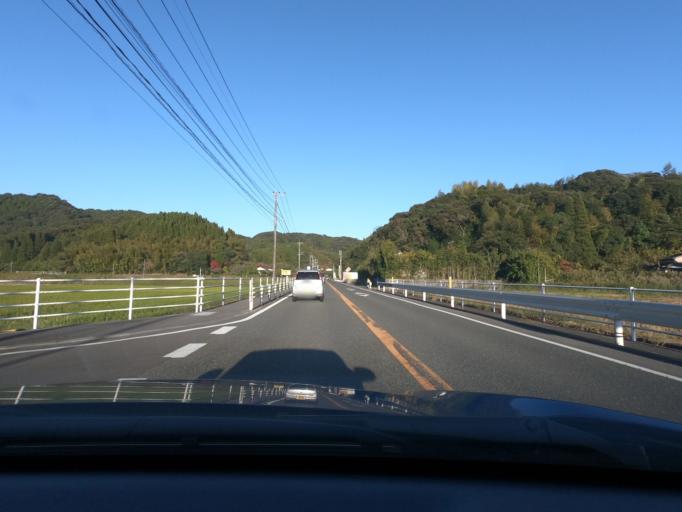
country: JP
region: Kagoshima
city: Satsumasendai
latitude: 31.8493
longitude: 130.2612
